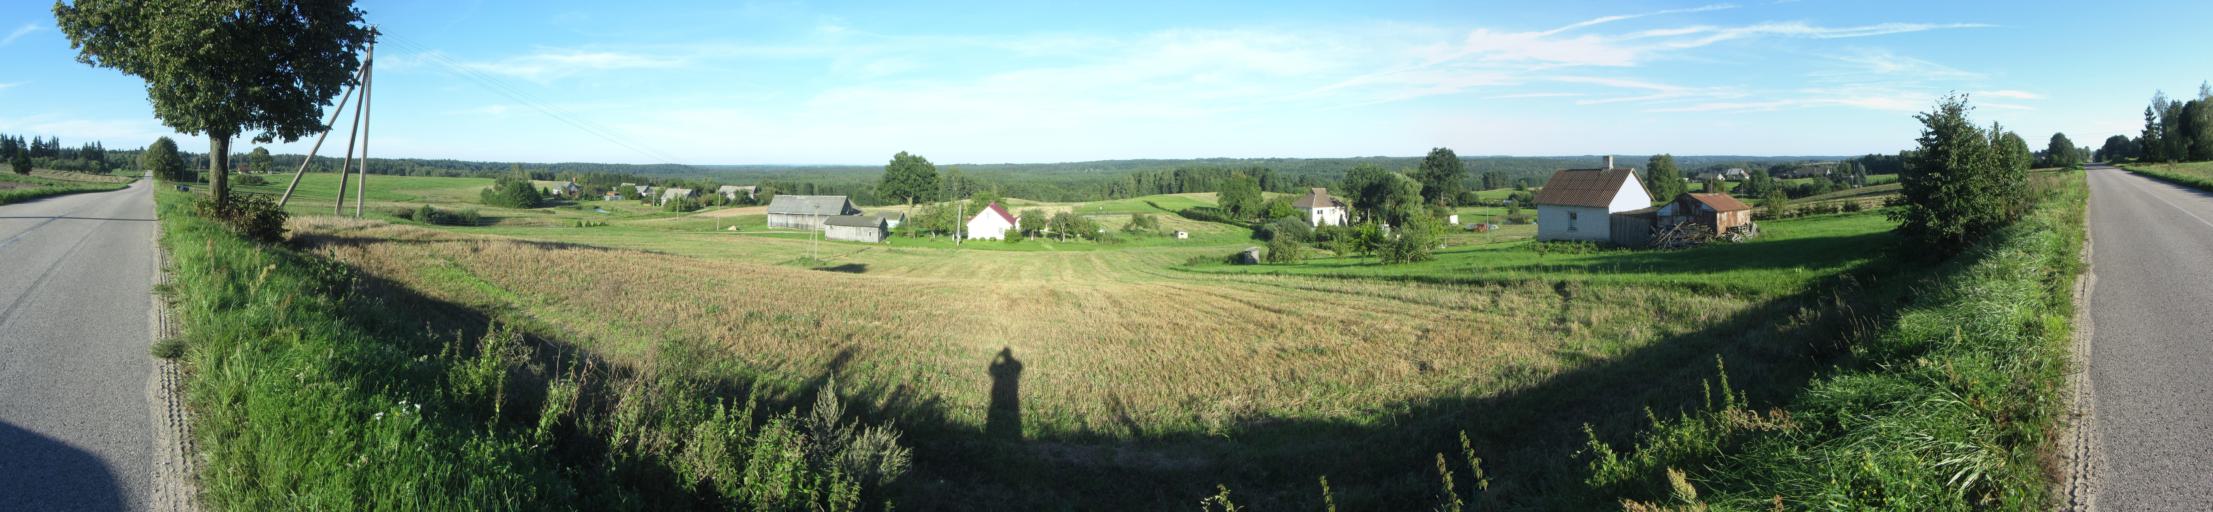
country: LT
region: Alytaus apskritis
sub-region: Alytus
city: Alytus
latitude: 54.4998
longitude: 24.0375
